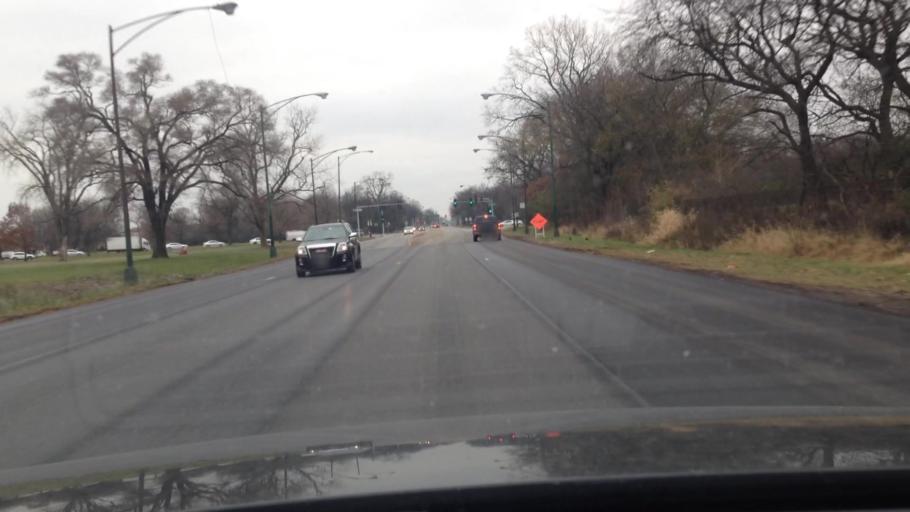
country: US
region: Illinois
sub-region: Cook County
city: River Grove
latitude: 41.9424
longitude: -87.8363
